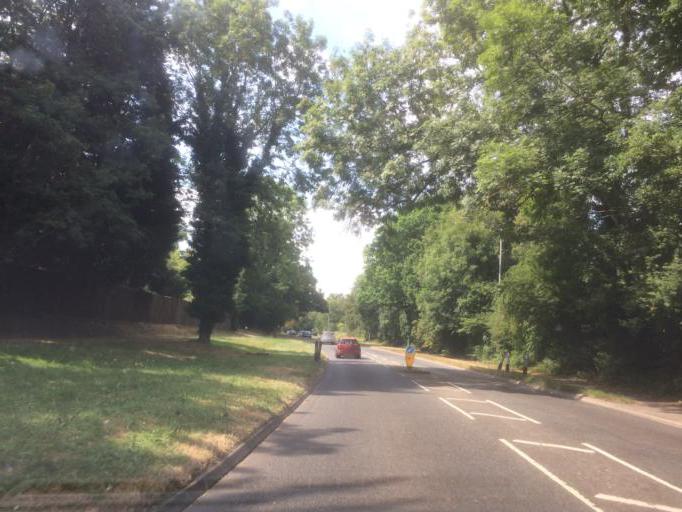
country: GB
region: England
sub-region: Buckinghamshire
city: Farnham Royal
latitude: 51.5641
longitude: -0.6154
